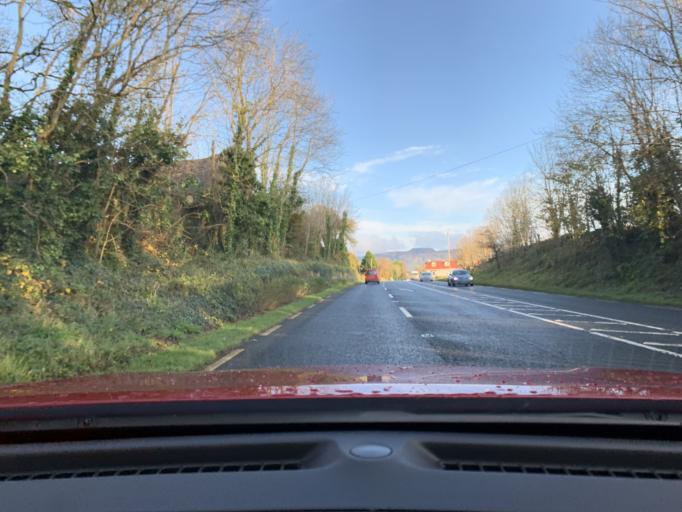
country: IE
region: Connaught
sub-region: Sligo
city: Sligo
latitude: 54.2918
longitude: -8.4740
